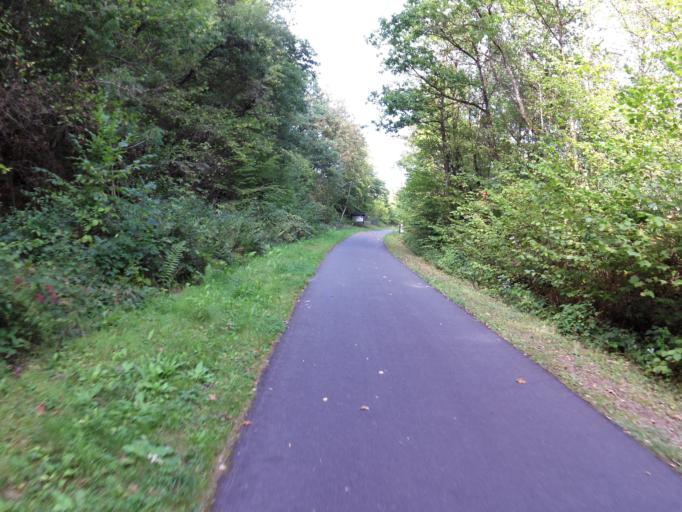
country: DE
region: Rheinland-Pfalz
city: Pronsfeld
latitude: 50.1578
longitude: 6.3329
